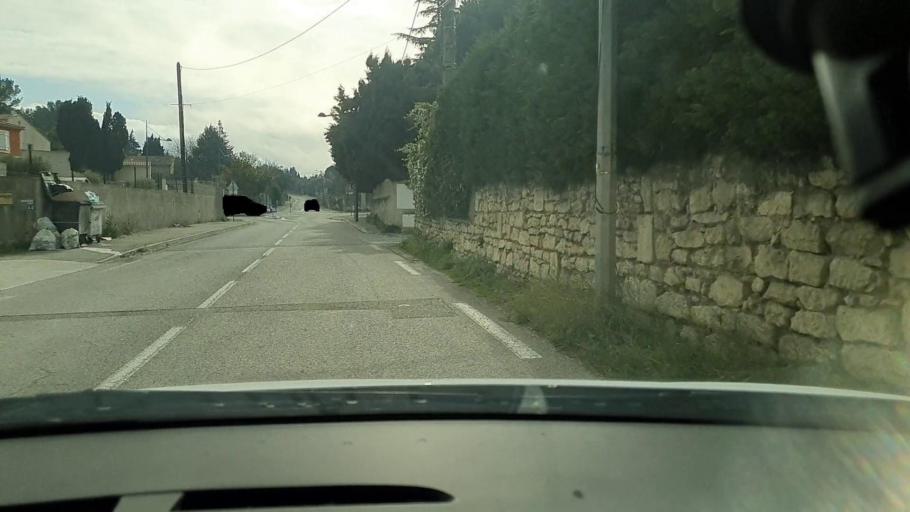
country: FR
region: Languedoc-Roussillon
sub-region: Departement du Gard
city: Beaucaire
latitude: 43.8170
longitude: 4.6299
